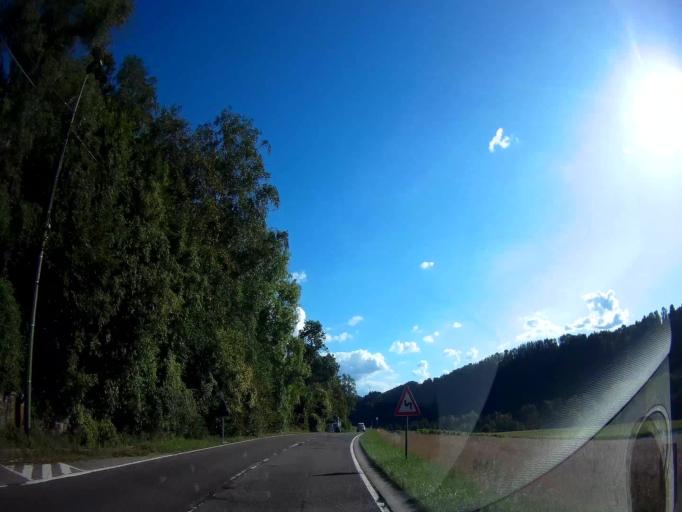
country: BE
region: Wallonia
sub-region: Province de Namur
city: Anhee
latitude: 50.2893
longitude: 4.8969
